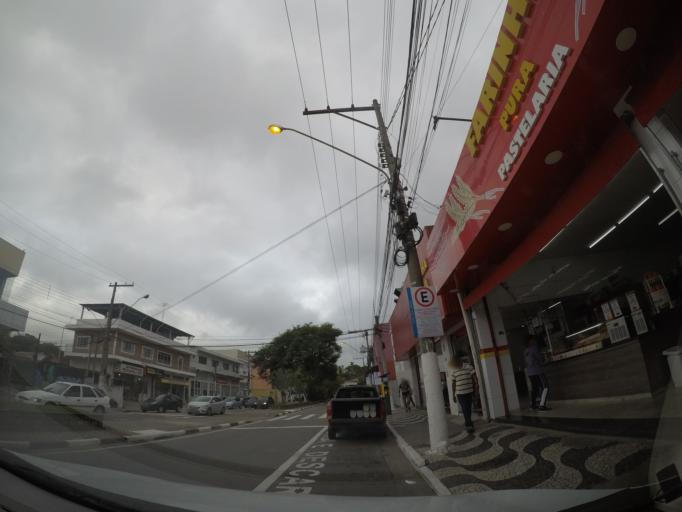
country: BR
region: Sao Paulo
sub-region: Aruja
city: Aruja
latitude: -23.3959
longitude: -46.3218
